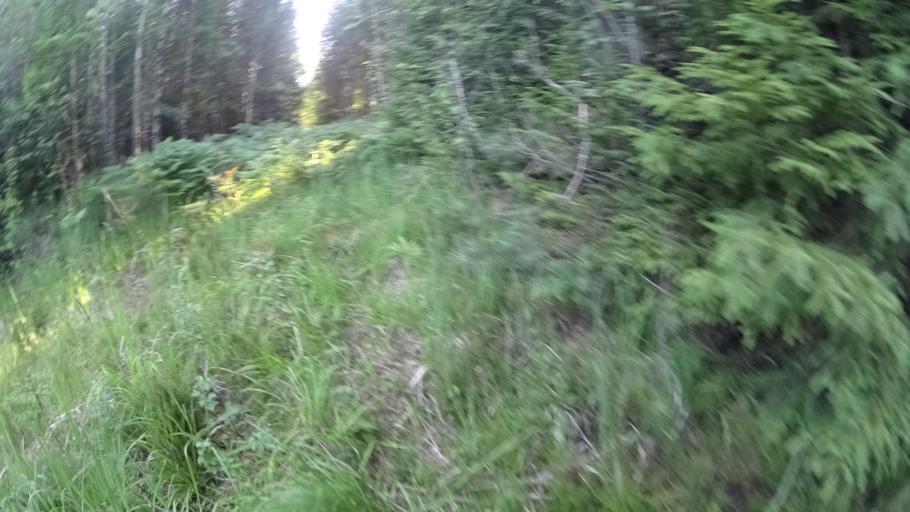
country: FI
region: Uusimaa
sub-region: Helsinki
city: Karkkila
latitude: 60.5925
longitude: 24.0931
